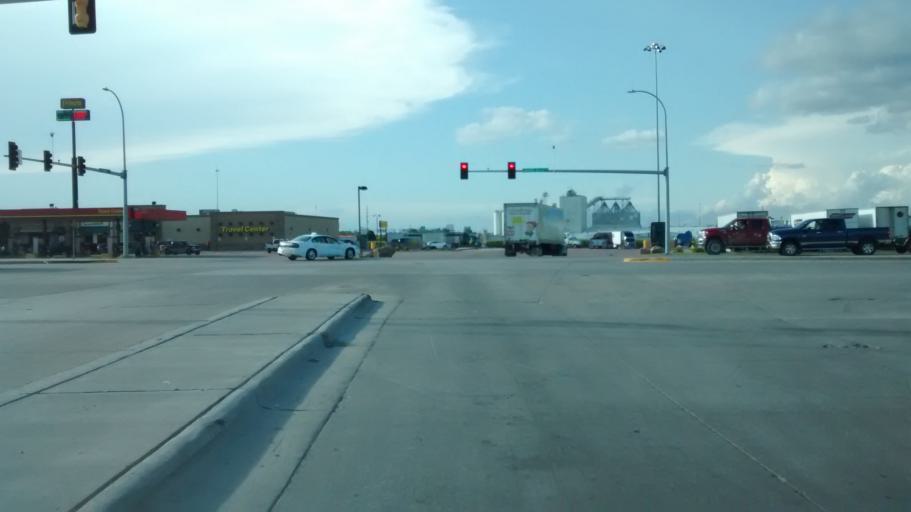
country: US
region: Iowa
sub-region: Woodbury County
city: Sergeant Bluff
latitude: 42.4345
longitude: -96.3722
